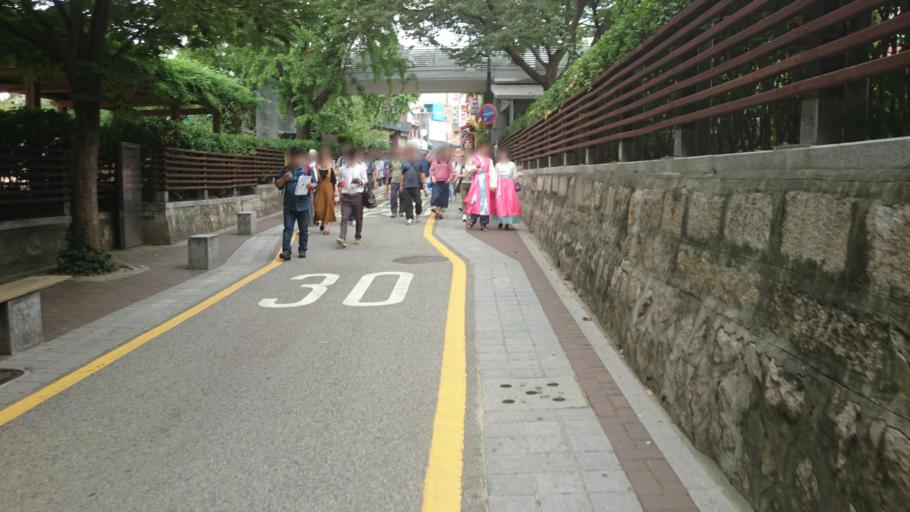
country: KR
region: Seoul
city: Seoul
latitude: 37.5780
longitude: 126.9823
